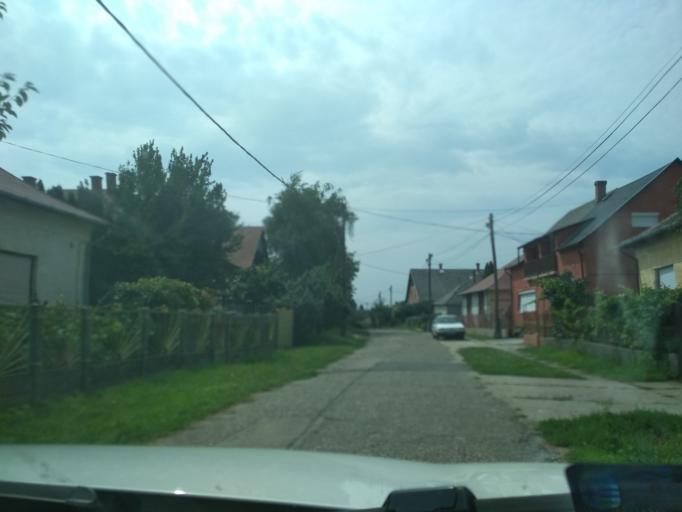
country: HU
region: Jasz-Nagykun-Szolnok
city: Tiszafured
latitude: 47.6126
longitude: 20.7681
